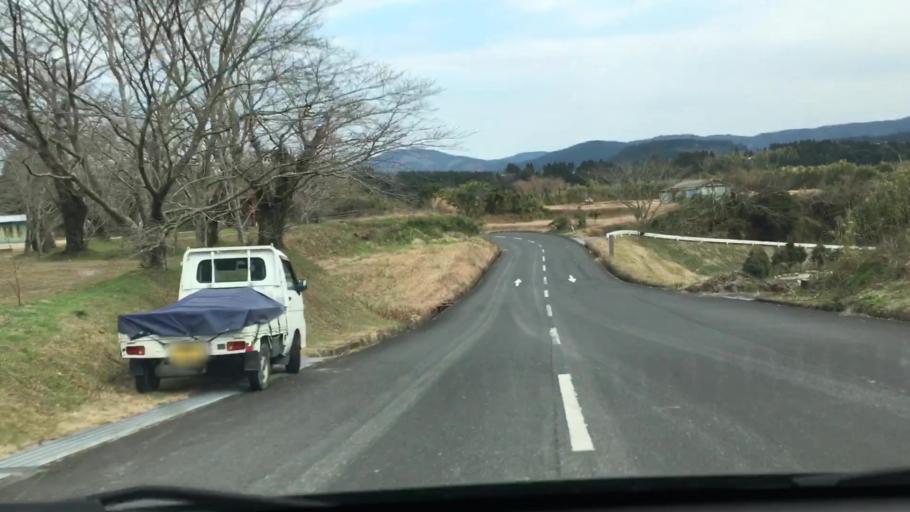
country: JP
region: Miyazaki
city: Kushima
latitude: 31.4964
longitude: 131.2347
